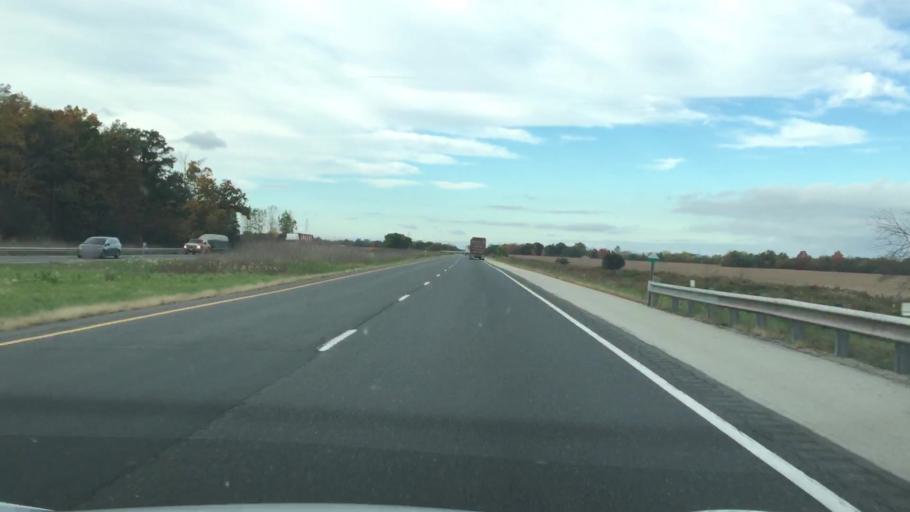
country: CA
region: Ontario
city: Delaware
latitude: 42.8986
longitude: -81.3886
